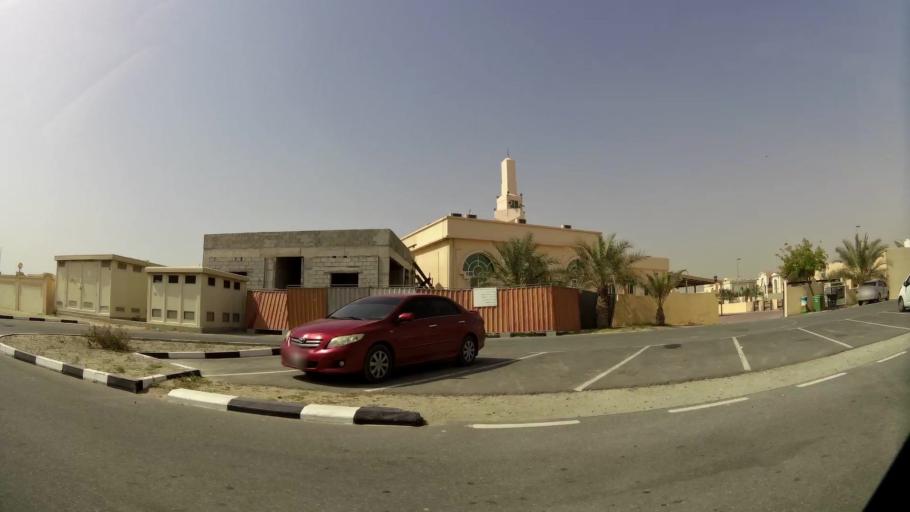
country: AE
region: Ash Shariqah
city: Sharjah
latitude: 25.2497
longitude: 55.4360
